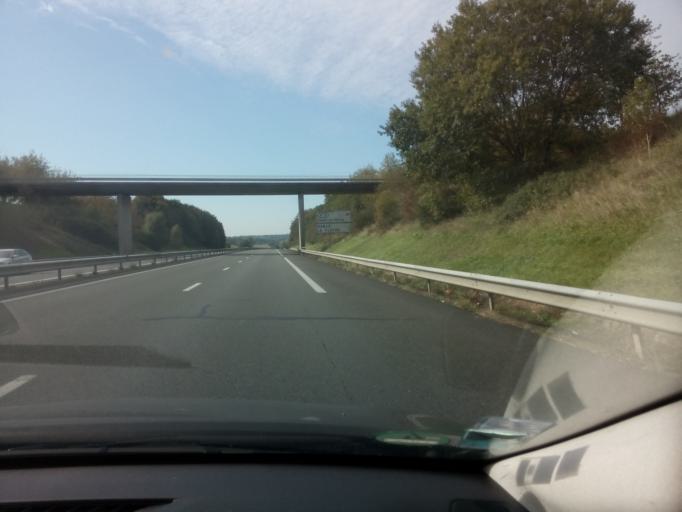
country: FR
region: Pays de la Loire
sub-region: Departement de la Sarthe
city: Etival-les-le-Mans
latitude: 47.9730
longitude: 0.0431
